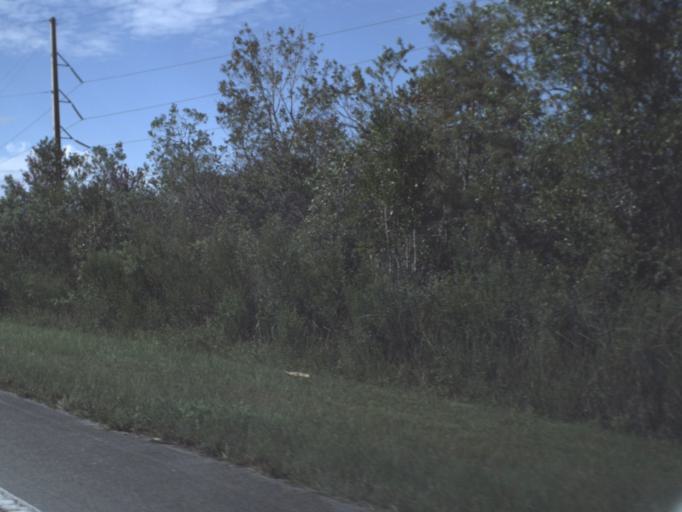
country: US
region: Florida
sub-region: Collier County
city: Lely Resort
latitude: 26.0064
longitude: -81.3465
